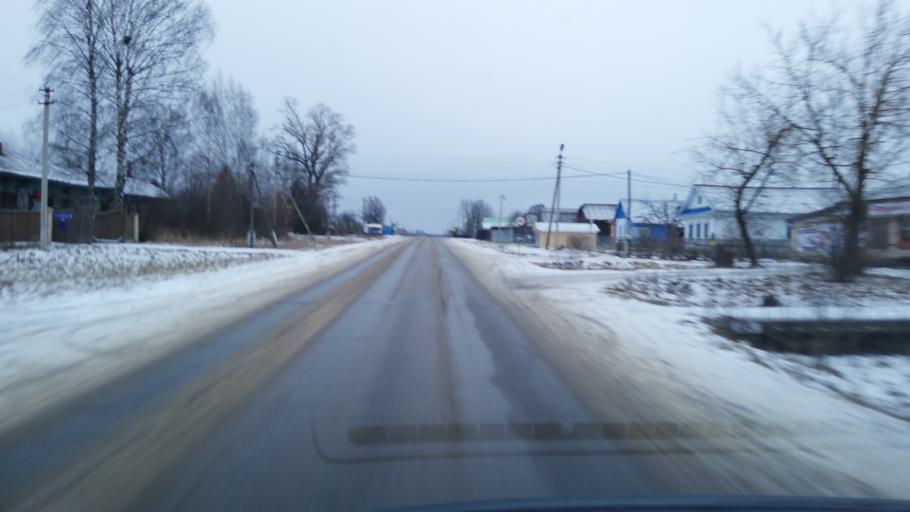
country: RU
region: Kostroma
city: Oktyabr'skiy
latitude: 57.7148
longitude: 41.1489
